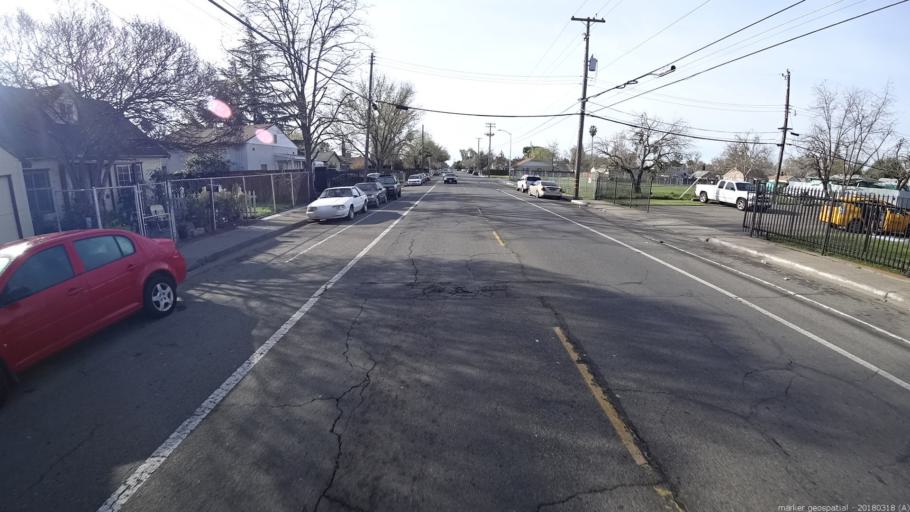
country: US
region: California
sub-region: Sacramento County
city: Parkway
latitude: 38.5316
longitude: -121.4647
